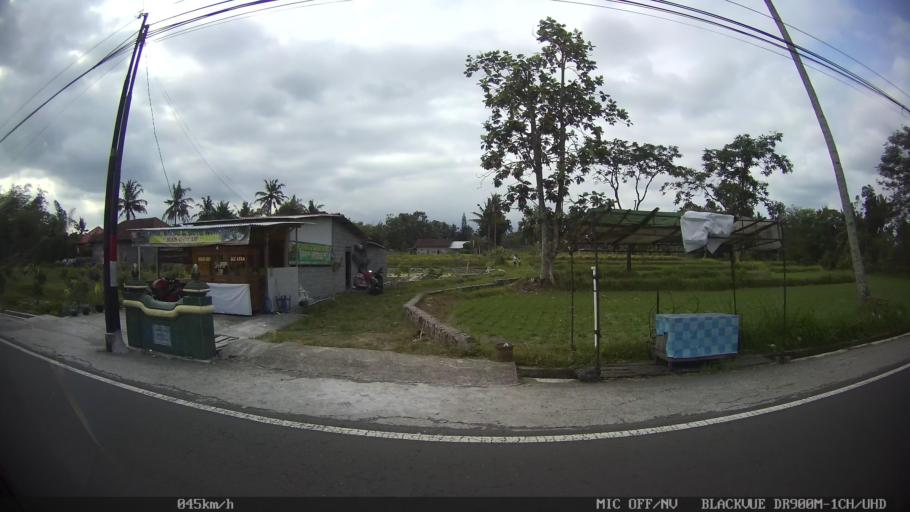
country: ID
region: Daerah Istimewa Yogyakarta
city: Sleman
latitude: -7.6831
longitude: 110.4264
